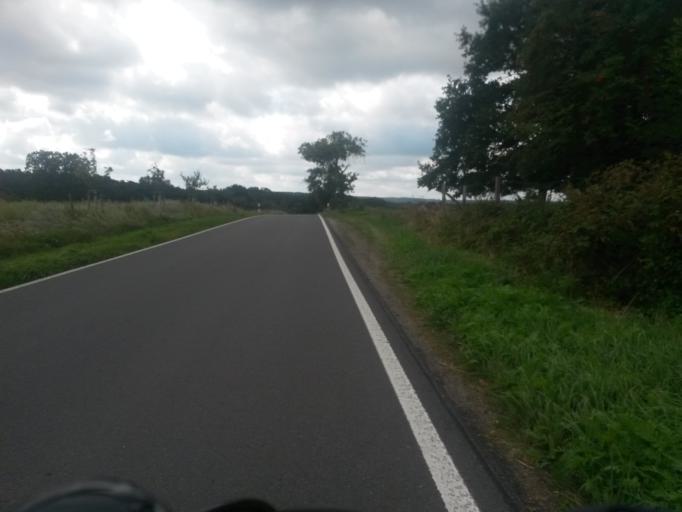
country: DE
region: Brandenburg
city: Angermunde
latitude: 53.0321
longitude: 13.9046
